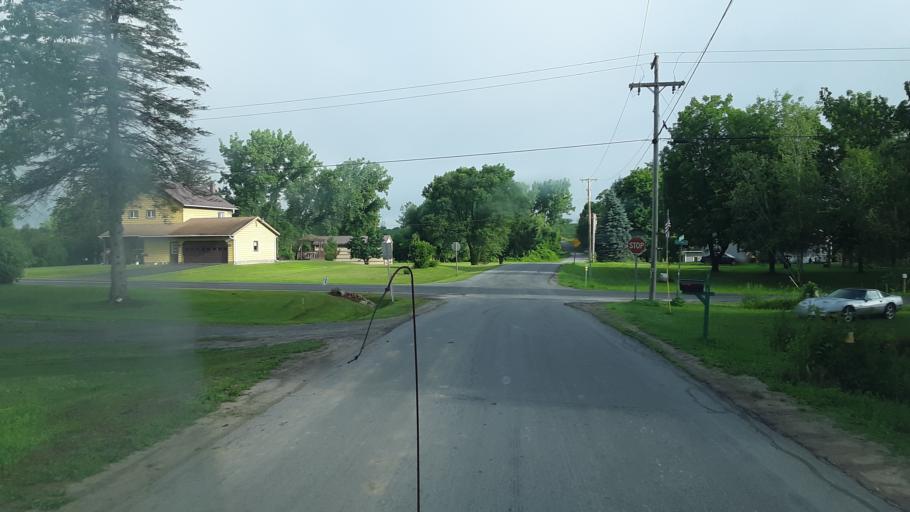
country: US
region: New York
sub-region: Montgomery County
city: Fonda
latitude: 42.8799
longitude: -74.3792
